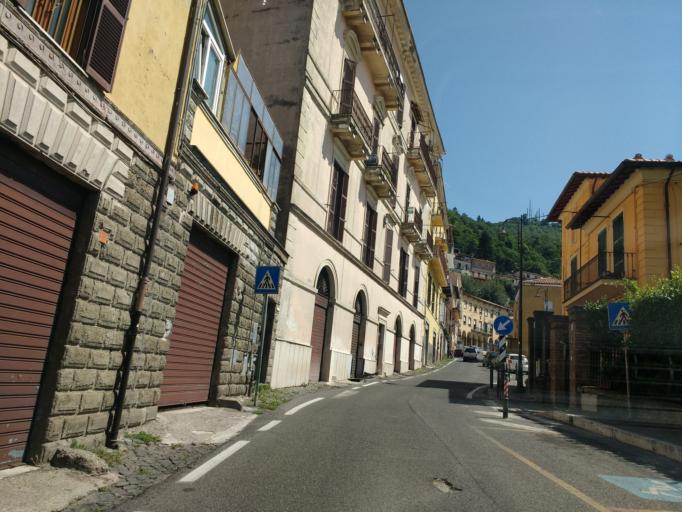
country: IT
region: Latium
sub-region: Citta metropolitana di Roma Capitale
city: Rocca di Papa
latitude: 41.7609
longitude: 12.7076
